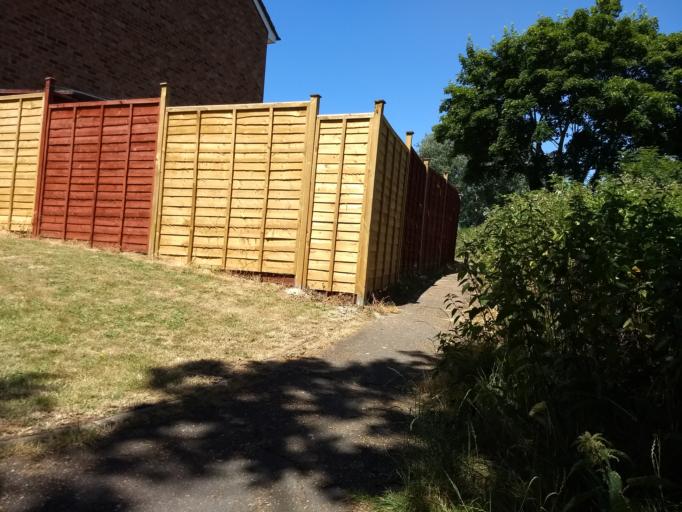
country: GB
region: England
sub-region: Isle of Wight
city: East Cowes
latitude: 50.7511
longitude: -1.2955
